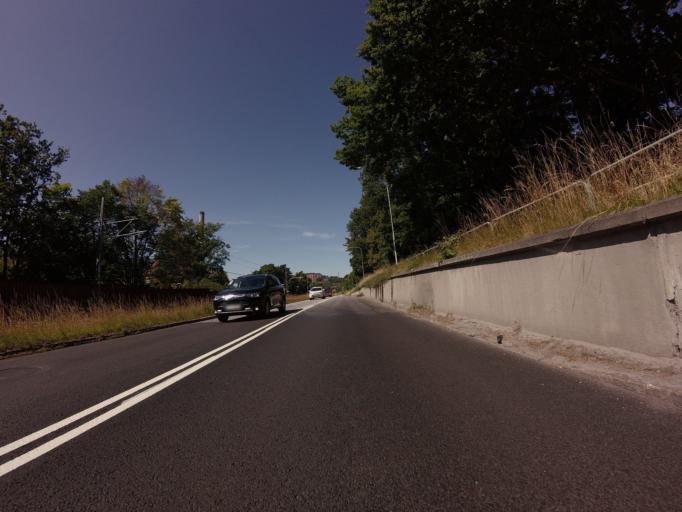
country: SE
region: Stockholm
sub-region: Nacka Kommun
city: Nacka
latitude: 59.3444
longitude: 18.1647
